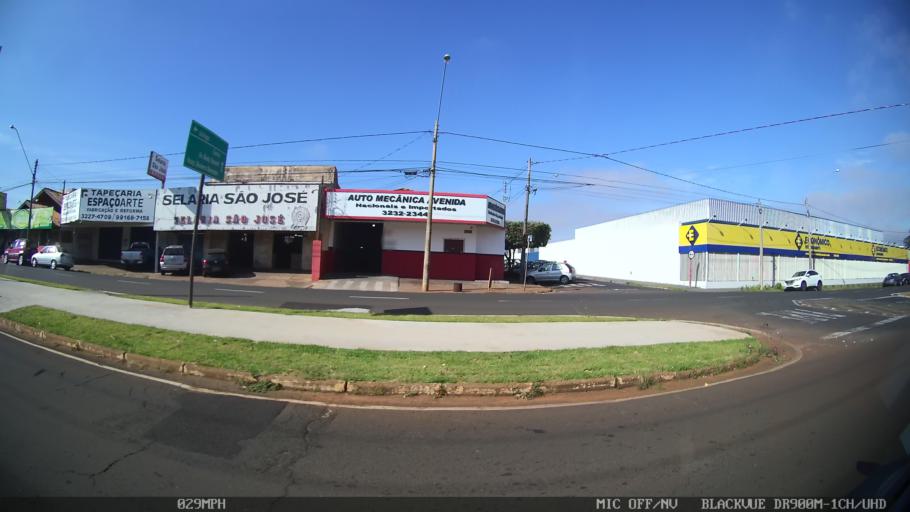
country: BR
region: Sao Paulo
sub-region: Sao Jose Do Rio Preto
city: Sao Jose do Rio Preto
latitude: -20.8108
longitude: -49.4028
